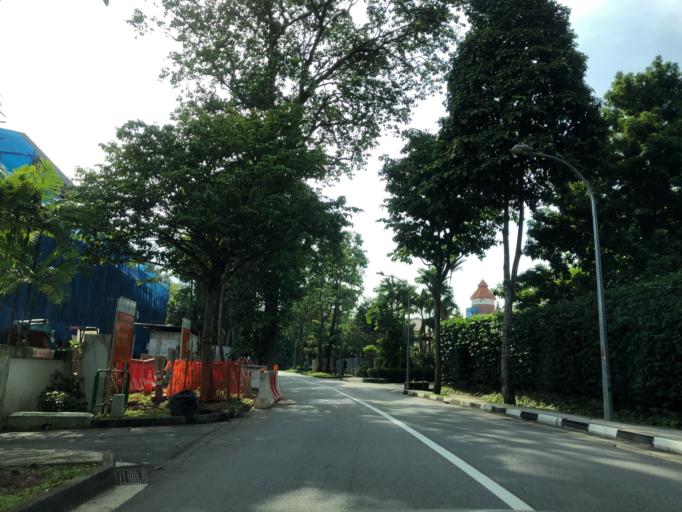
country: SG
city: Singapore
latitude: 1.3152
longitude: 103.8240
